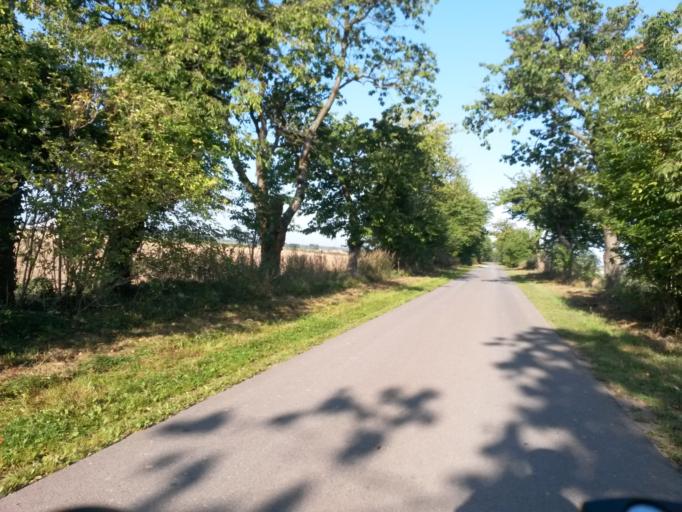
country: DE
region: Brandenburg
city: Templin
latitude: 53.1262
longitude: 13.4800
